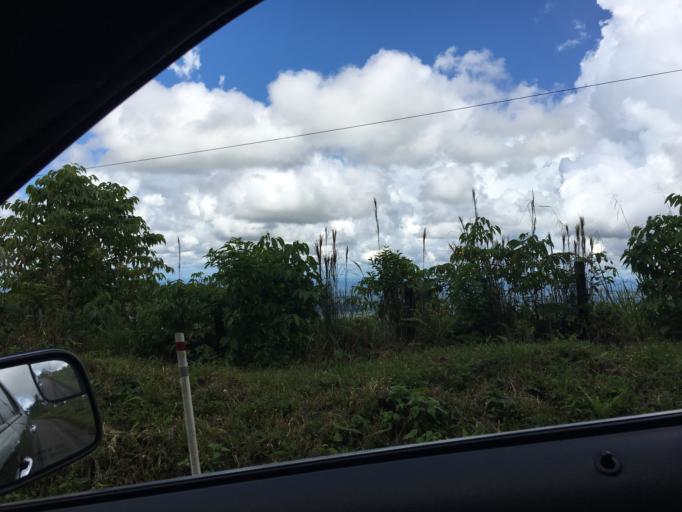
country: EC
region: Napo
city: Archidona
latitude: -0.7355
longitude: -77.5127
